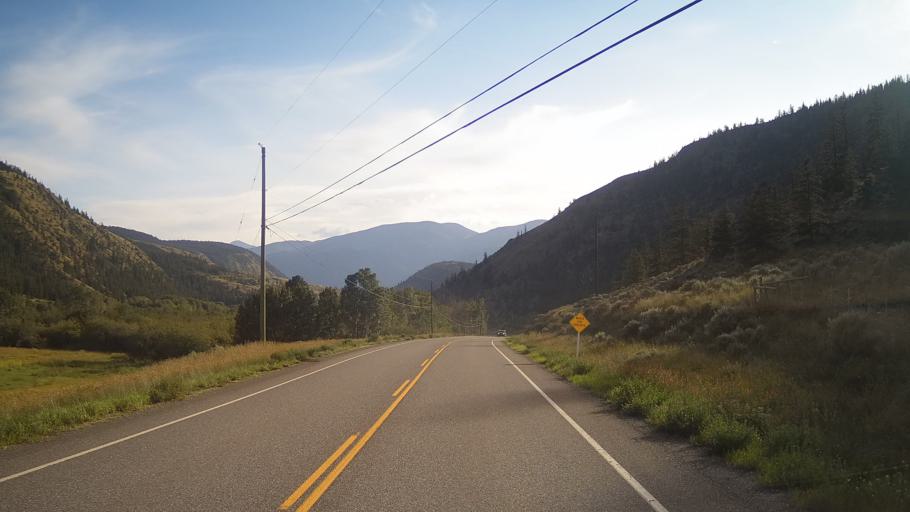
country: CA
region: British Columbia
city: Lillooet
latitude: 50.8951
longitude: -121.7973
